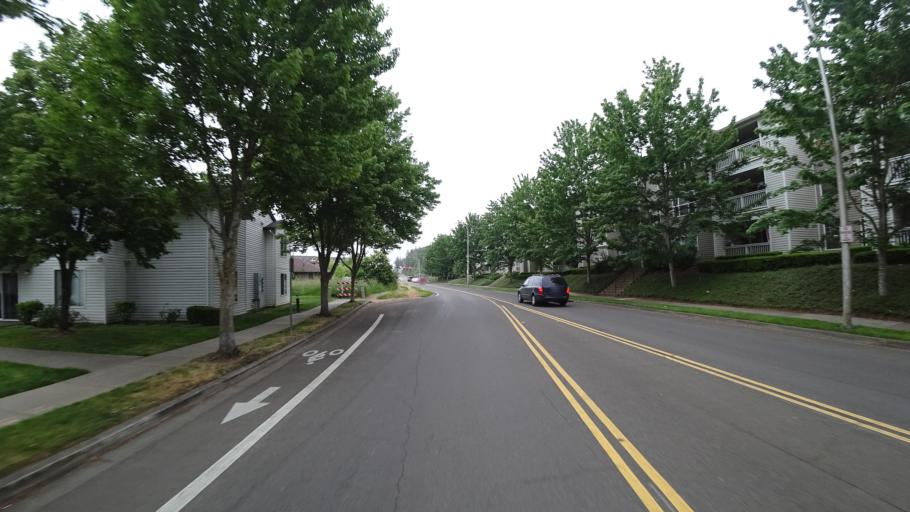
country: US
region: Oregon
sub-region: Washington County
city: Rockcreek
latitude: 45.5271
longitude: -122.8913
